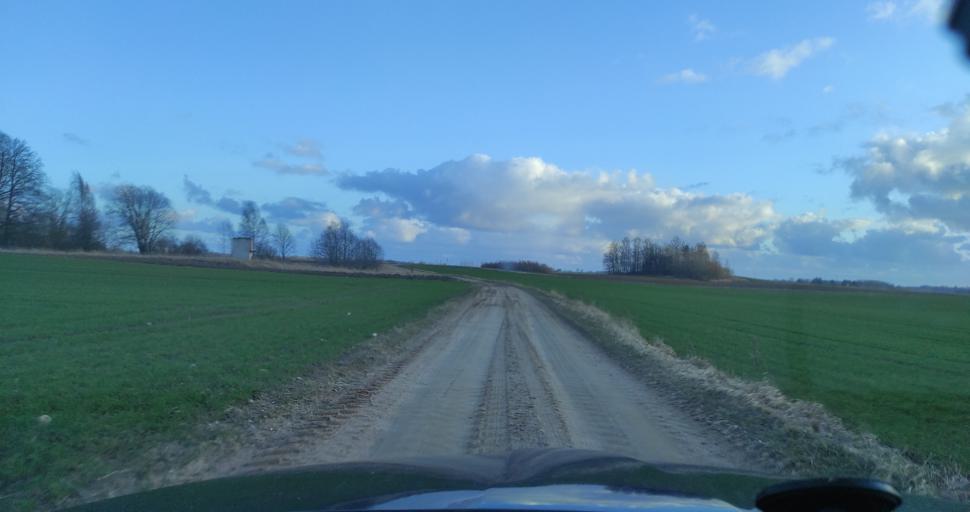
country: LV
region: Aizpute
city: Aizpute
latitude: 56.8592
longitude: 21.7613
